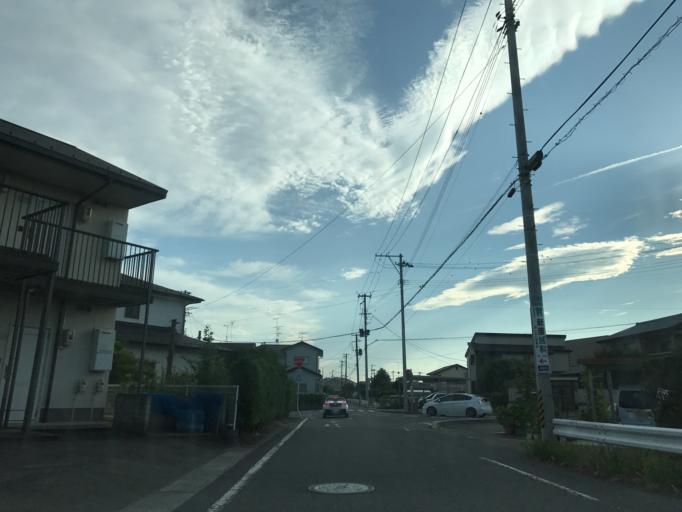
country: JP
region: Fukushima
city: Sukagawa
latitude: 37.3053
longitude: 140.3598
